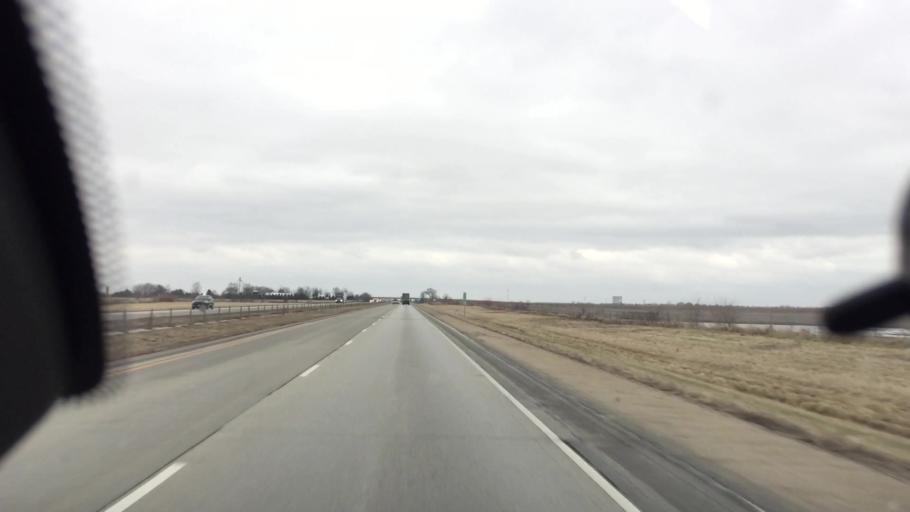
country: US
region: Illinois
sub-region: Vermilion County
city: Oakwood
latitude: 40.1245
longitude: -87.8239
